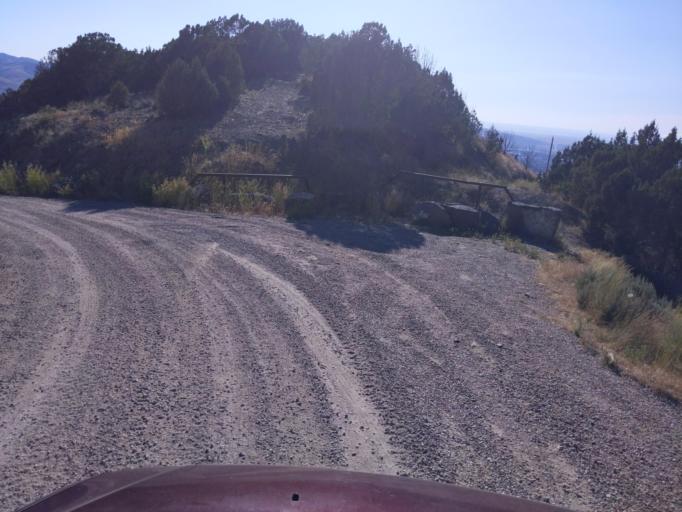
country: US
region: Idaho
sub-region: Bannock County
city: Pocatello
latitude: 42.8519
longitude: -112.3779
